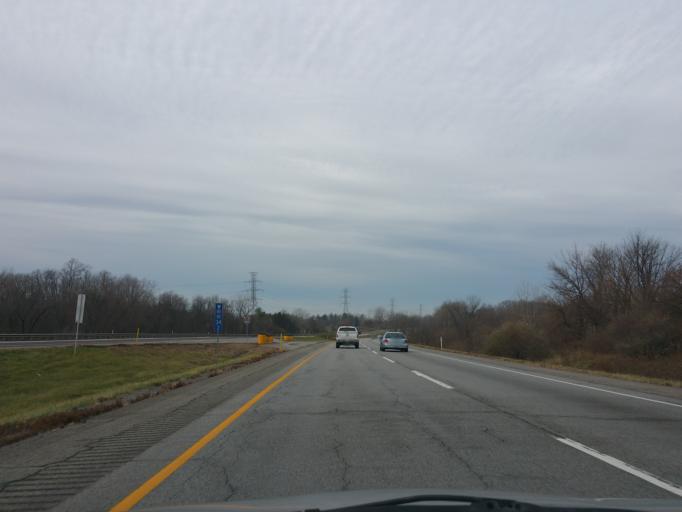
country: US
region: Indiana
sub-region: Porter County
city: Chesterton
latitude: 41.5711
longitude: -86.9855
